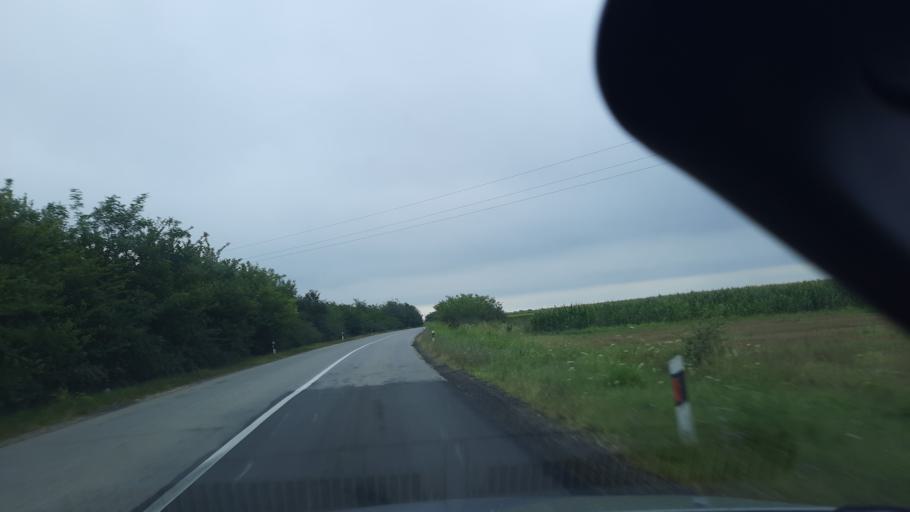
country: RS
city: Farkazdin
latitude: 45.2031
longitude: 20.4282
